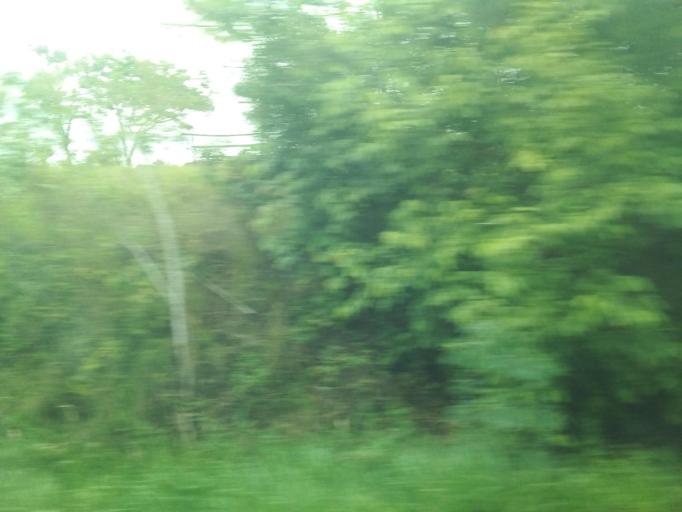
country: BR
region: Maranhao
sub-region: Vitoria Do Mearim
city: Vitoria do Mearim
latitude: -3.5834
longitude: -45.0491
